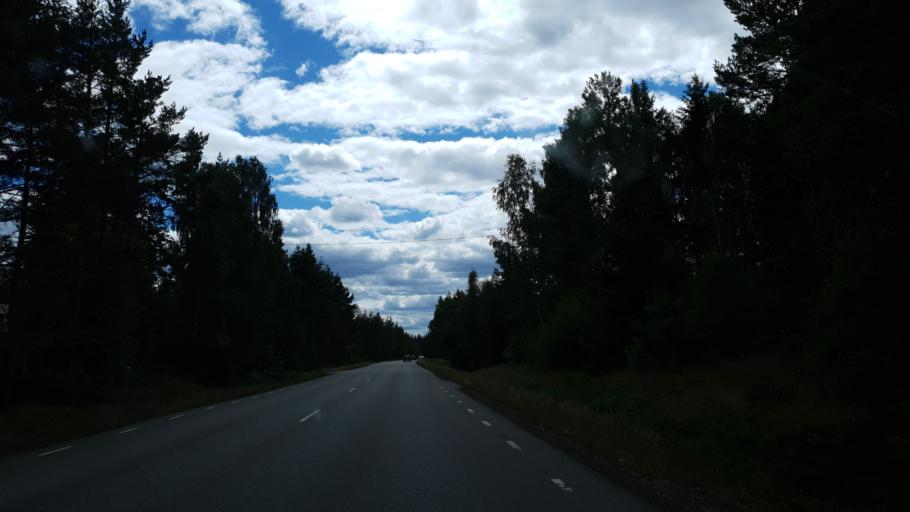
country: SE
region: Kronoberg
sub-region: Uppvidinge Kommun
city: Lenhovda
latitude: 56.9393
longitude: 15.5830
